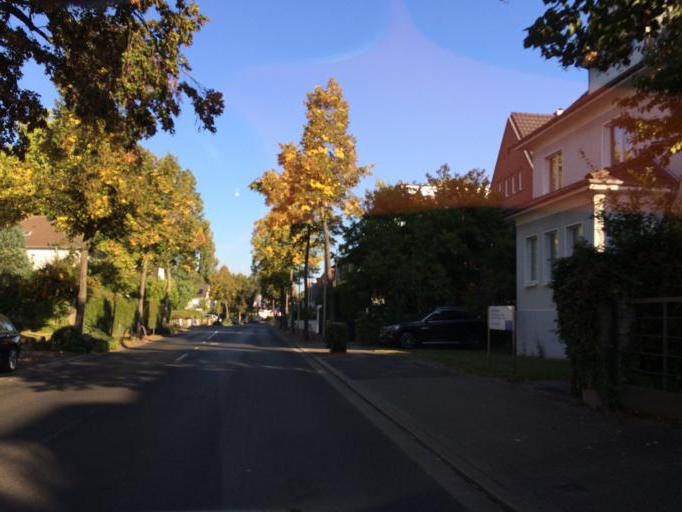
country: DE
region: North Rhine-Westphalia
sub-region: Regierungsbezirk Koln
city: Konigswinter
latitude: 50.6926
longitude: 7.1640
